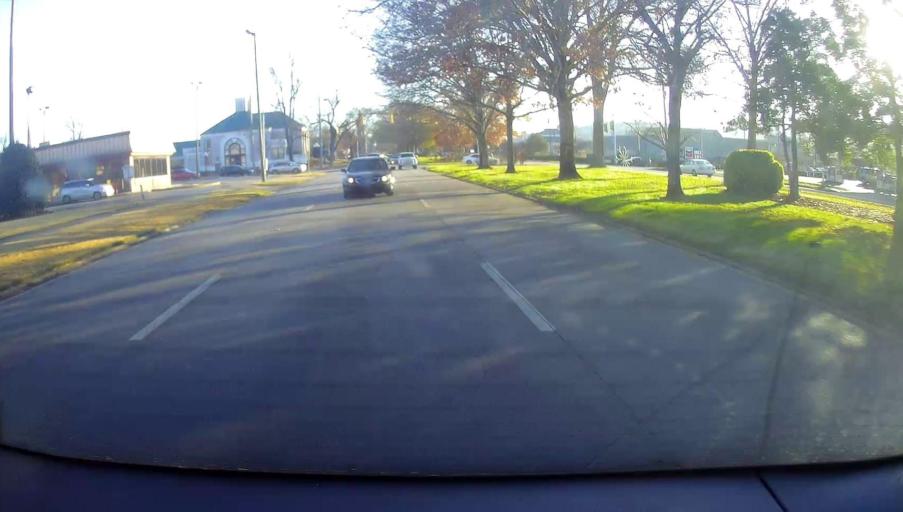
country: US
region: Alabama
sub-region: Calhoun County
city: Anniston
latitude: 33.6644
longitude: -85.8266
